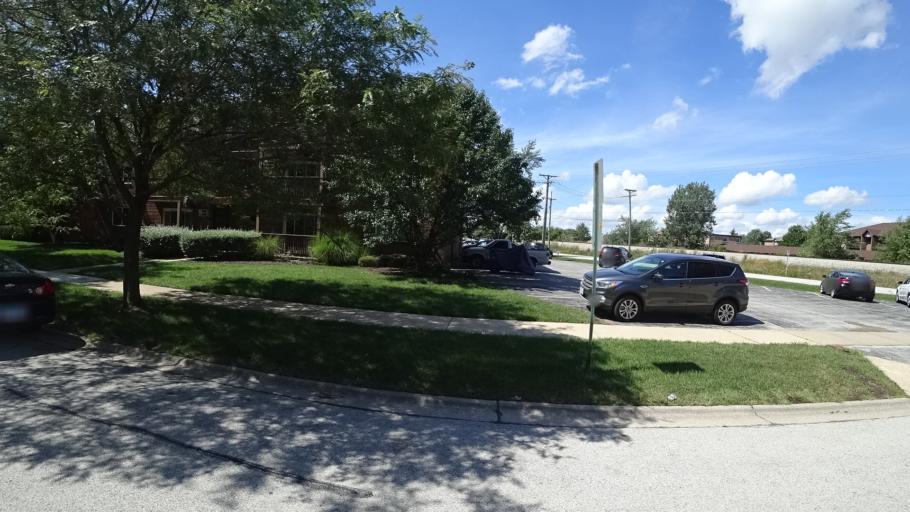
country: US
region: Illinois
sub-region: Cook County
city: Tinley Park
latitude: 41.5719
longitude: -87.7910
